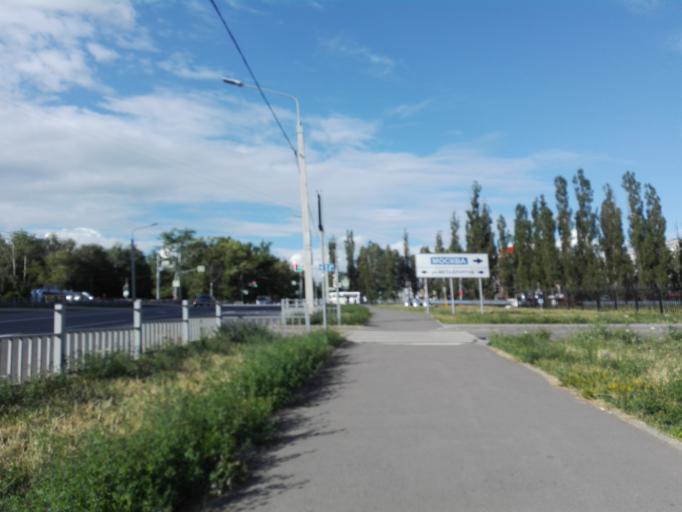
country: RU
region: Orjol
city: Orel
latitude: 53.0162
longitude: 36.1351
